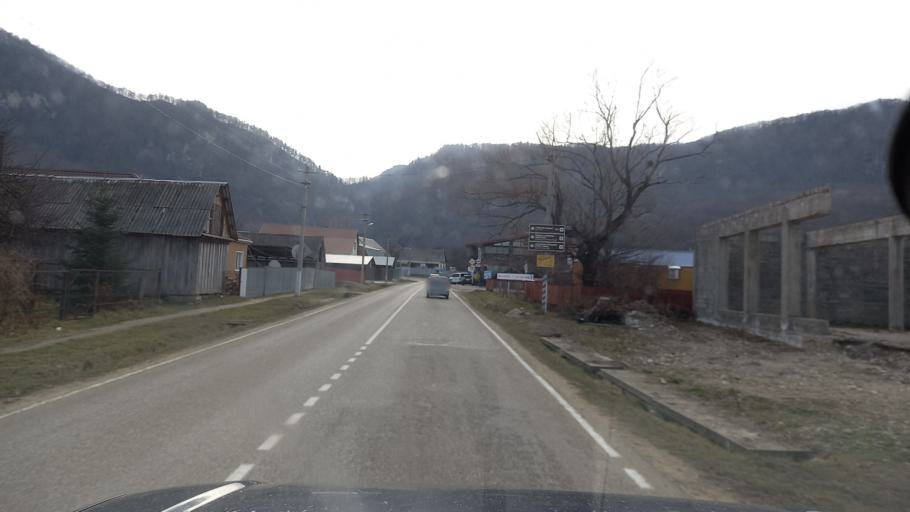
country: RU
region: Krasnodarskiy
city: Neftegorsk
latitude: 44.2315
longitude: 39.9020
